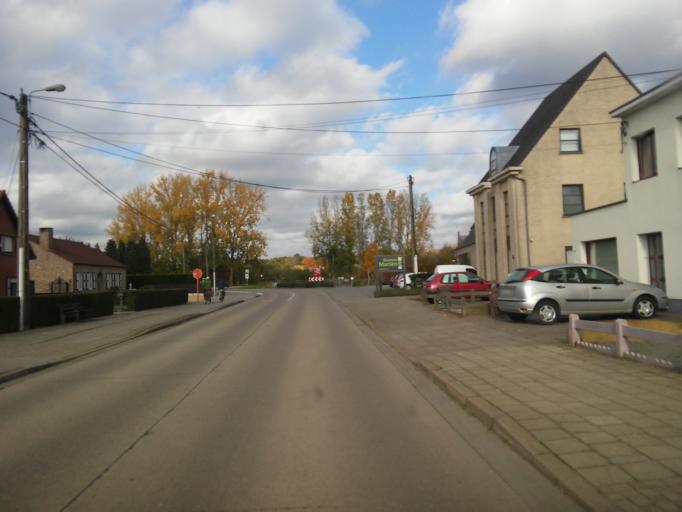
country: BE
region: Flanders
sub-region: Provincie Antwerpen
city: Berlaar
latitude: 51.1223
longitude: 4.6573
